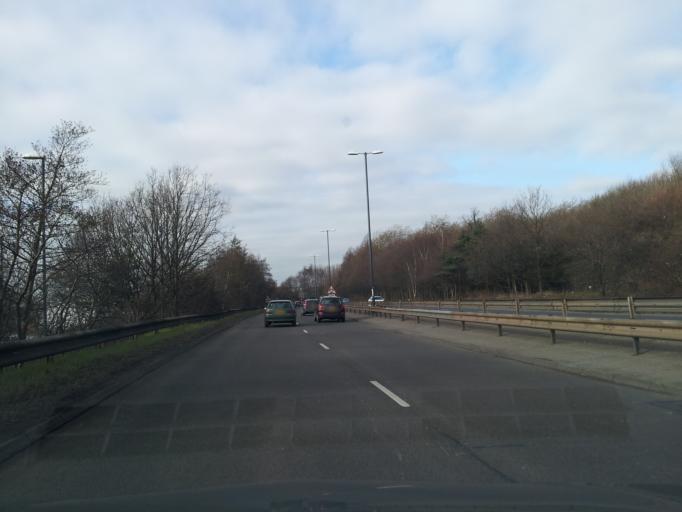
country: GB
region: England
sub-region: Derby
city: Derby
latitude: 52.9209
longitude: -1.4480
